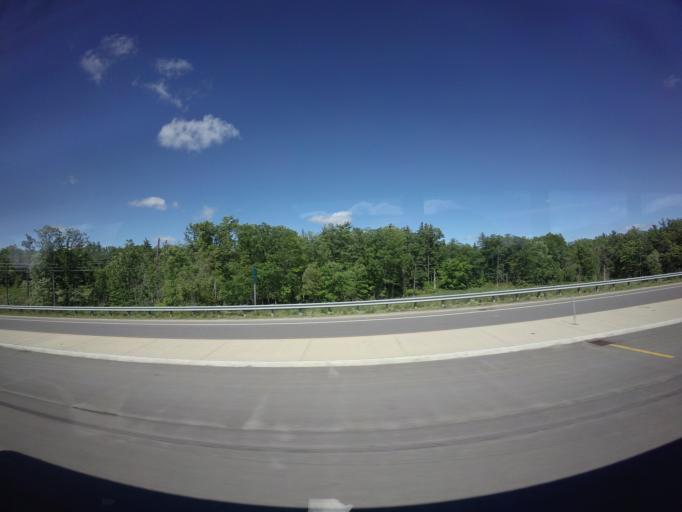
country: US
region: New Hampshire
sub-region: Rockingham County
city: Londonderry
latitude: 42.9205
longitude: -71.3739
